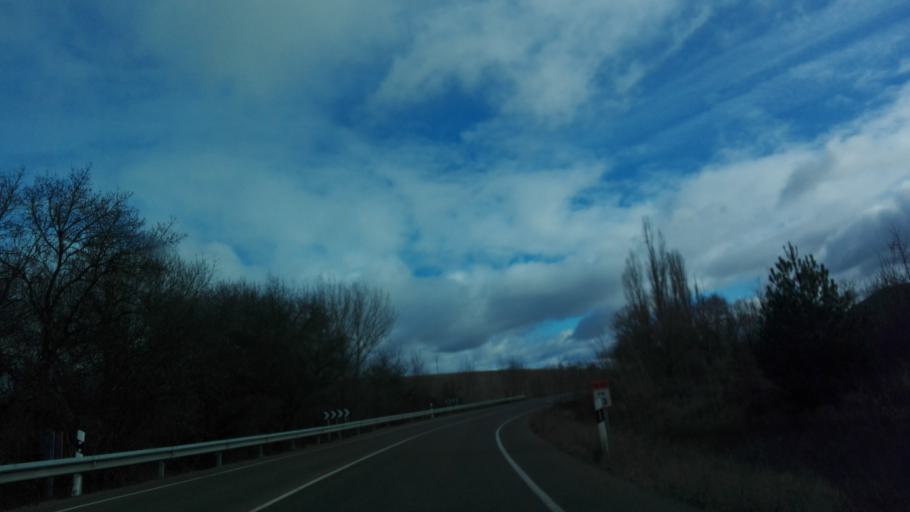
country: ES
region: Navarre
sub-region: Provincia de Navarra
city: Lizoain
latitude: 42.7817
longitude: -1.4584
